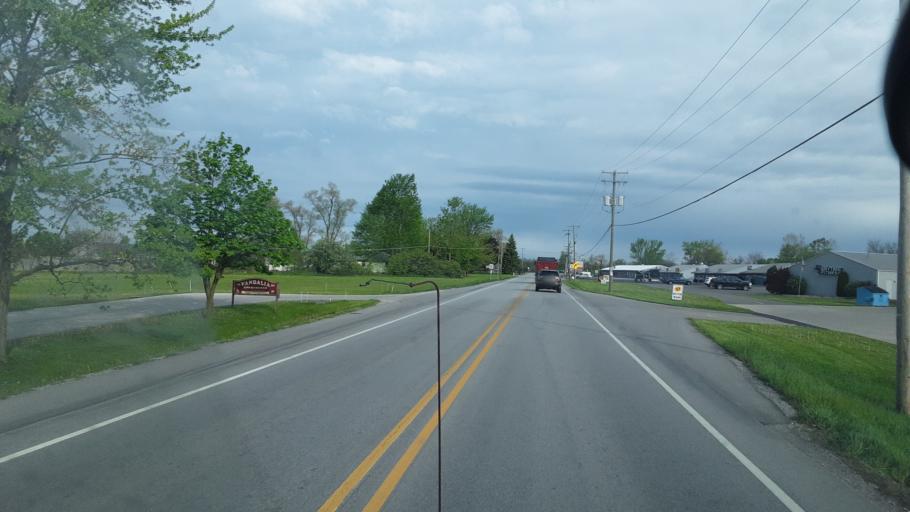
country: US
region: Indiana
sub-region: Whitley County
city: Churubusco
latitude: 41.2390
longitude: -85.3271
